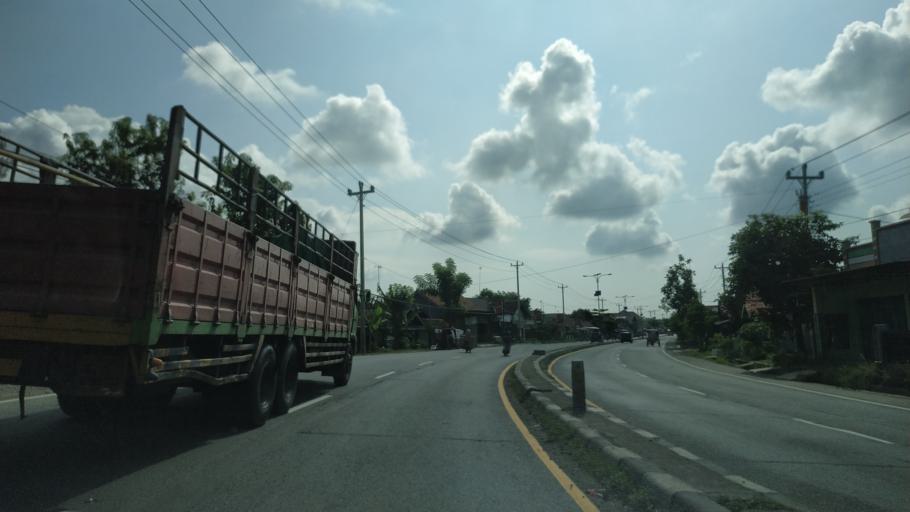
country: ID
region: Central Java
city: Comal
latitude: -6.8895
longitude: 109.5442
